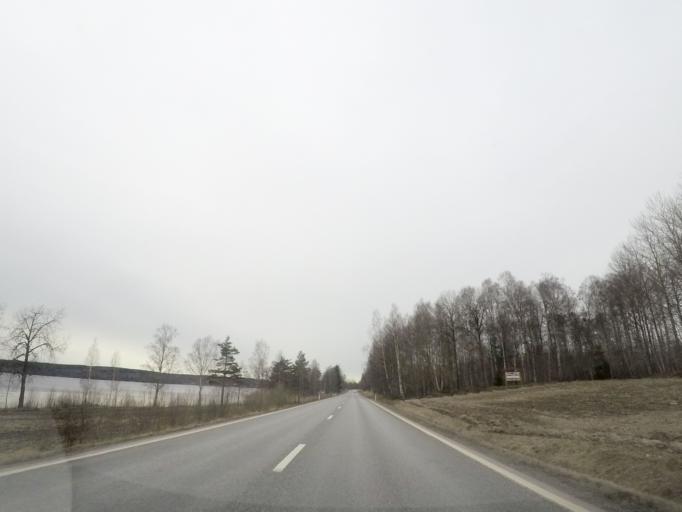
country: SE
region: Vaestmanland
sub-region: Skinnskattebergs Kommun
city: Skinnskatteberg
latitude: 59.8114
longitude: 15.7042
